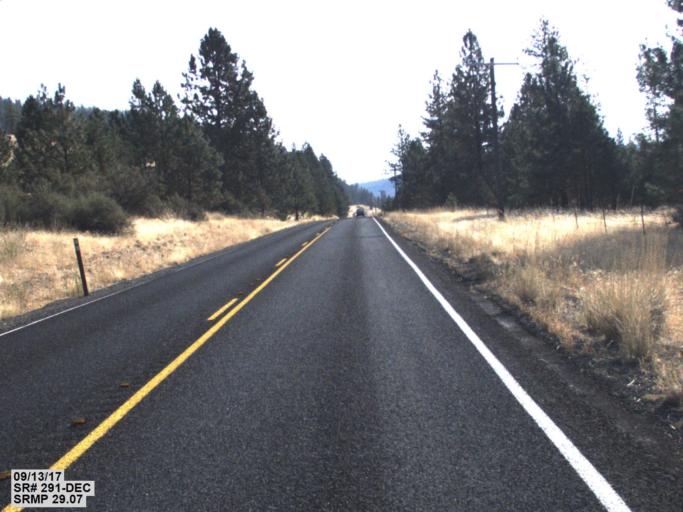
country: US
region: Washington
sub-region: Spokane County
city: Fairchild Air Force Base
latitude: 47.8391
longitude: -117.7755
